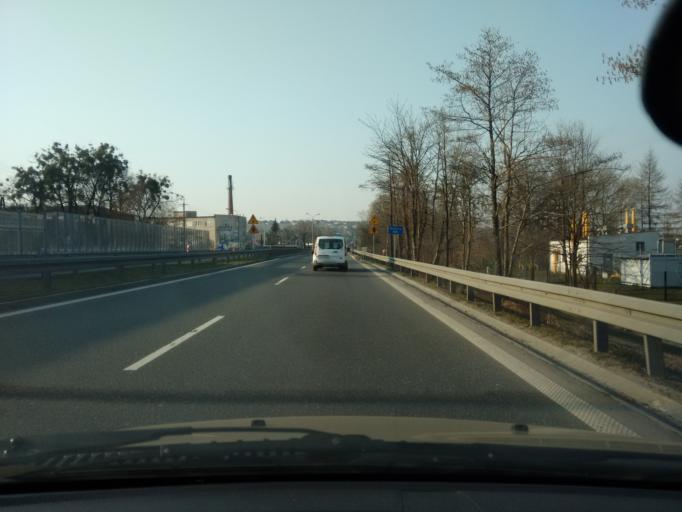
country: PL
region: Silesian Voivodeship
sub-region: Powiat cieszynski
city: Skoczow
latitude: 49.8000
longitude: 18.7924
